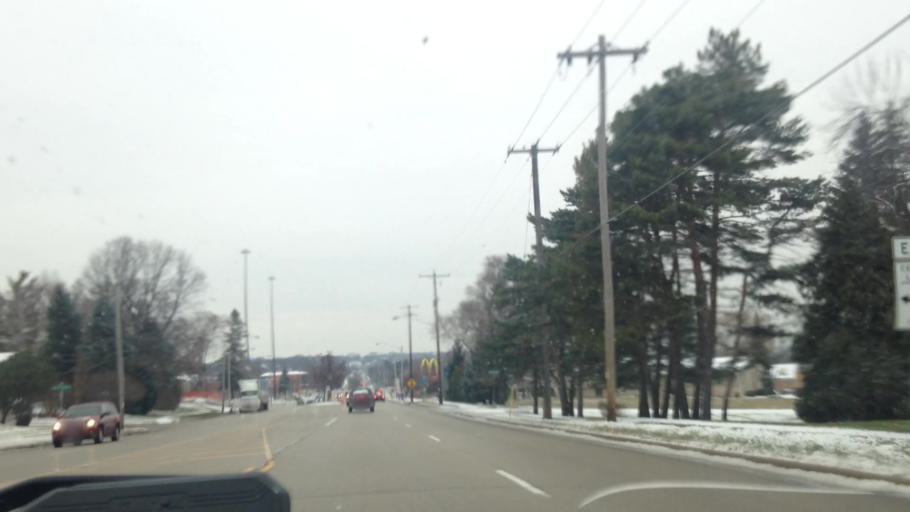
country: US
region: Wisconsin
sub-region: Waukesha County
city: Menomonee Falls
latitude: 43.1667
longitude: -88.1039
